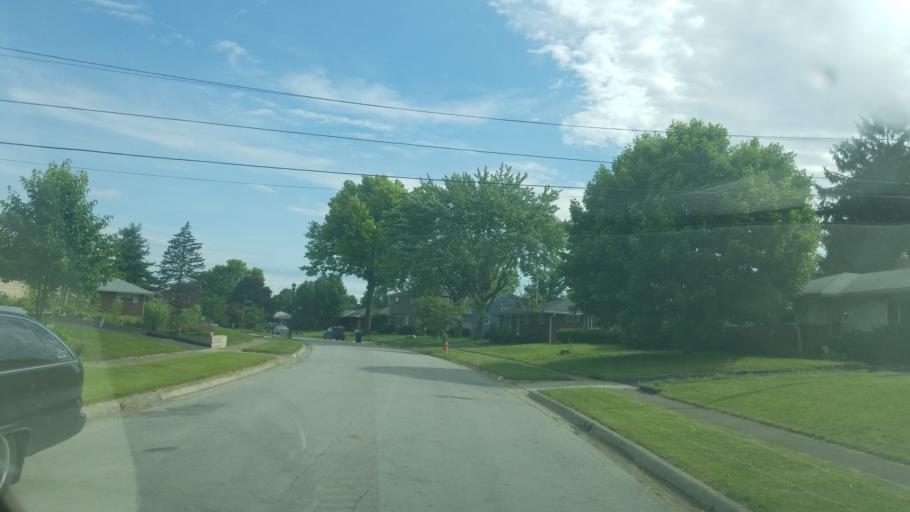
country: US
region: Ohio
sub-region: Franklin County
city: Worthington
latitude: 40.0552
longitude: -82.9913
